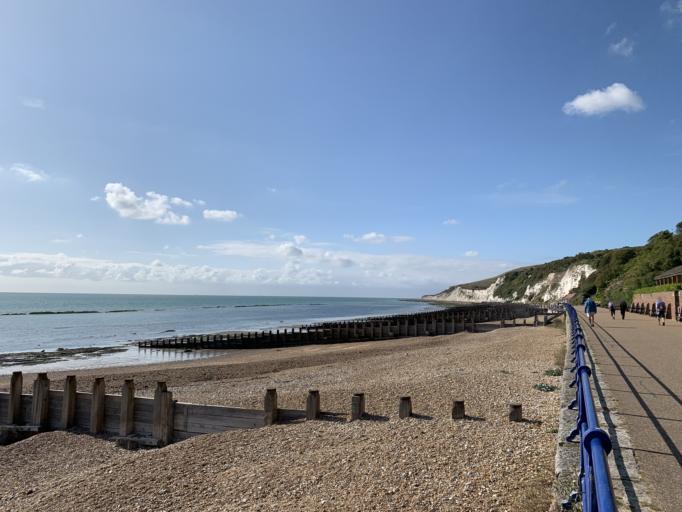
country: GB
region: England
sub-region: East Sussex
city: Eastbourne
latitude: 50.7553
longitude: 0.2756
